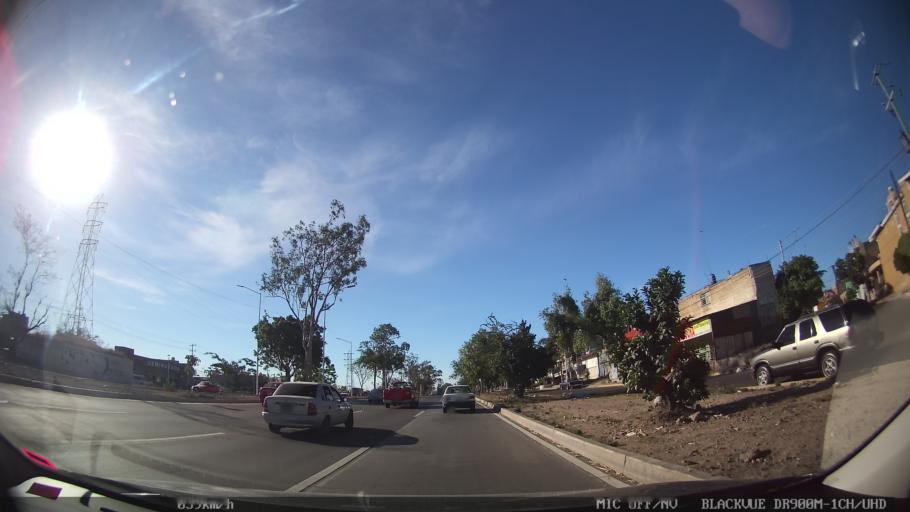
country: MX
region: Jalisco
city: Tlaquepaque
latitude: 20.7024
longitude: -103.2809
